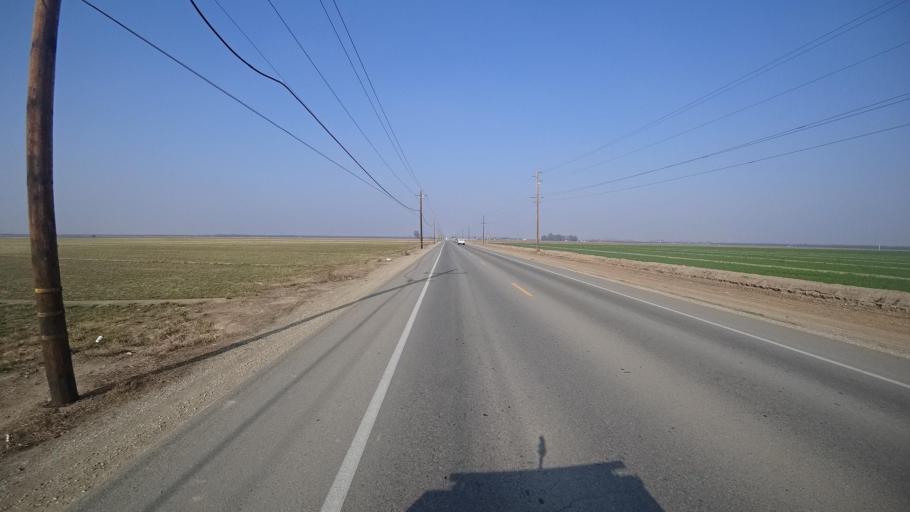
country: US
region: California
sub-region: Kern County
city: Greenfield
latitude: 35.1992
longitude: -119.1098
